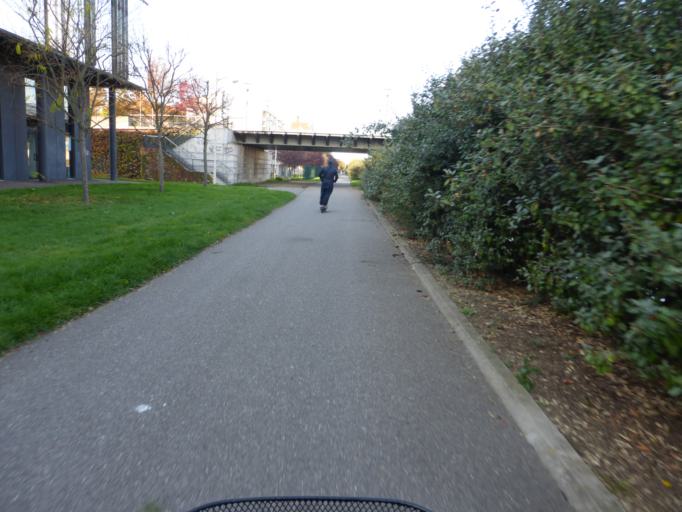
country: FR
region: Lorraine
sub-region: Departement de Meurthe-et-Moselle
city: Nancy
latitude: 48.6869
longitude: 6.1969
